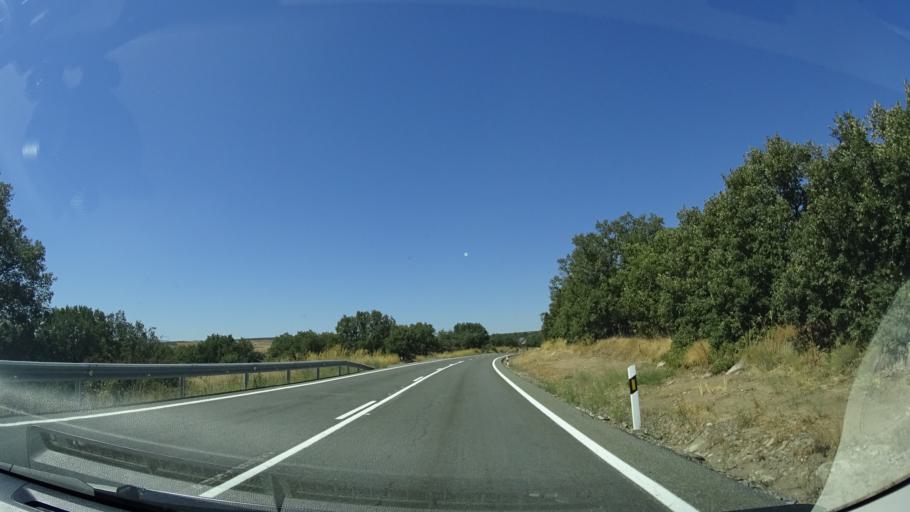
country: ES
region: Castille and Leon
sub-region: Provincia de Avila
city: Navalperal de Pinares
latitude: 40.5925
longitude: -4.4610
